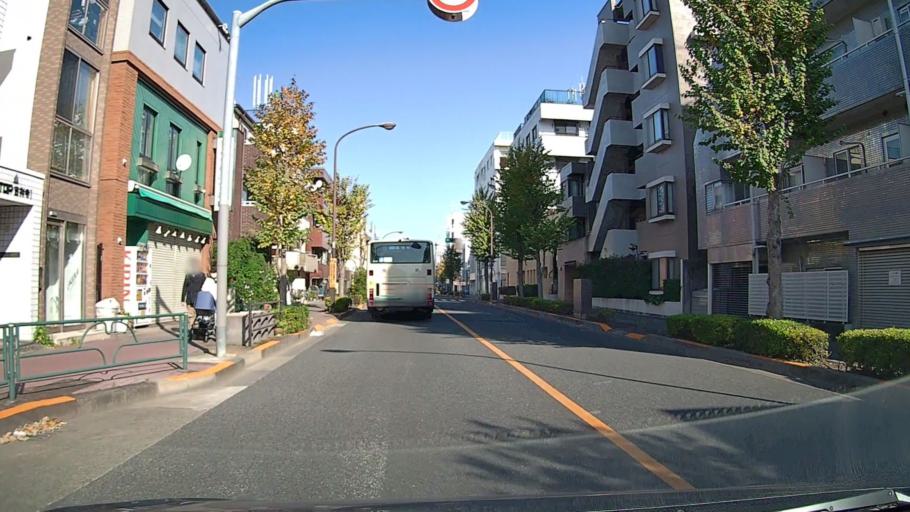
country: JP
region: Tokyo
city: Musashino
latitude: 35.7102
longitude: 139.5808
